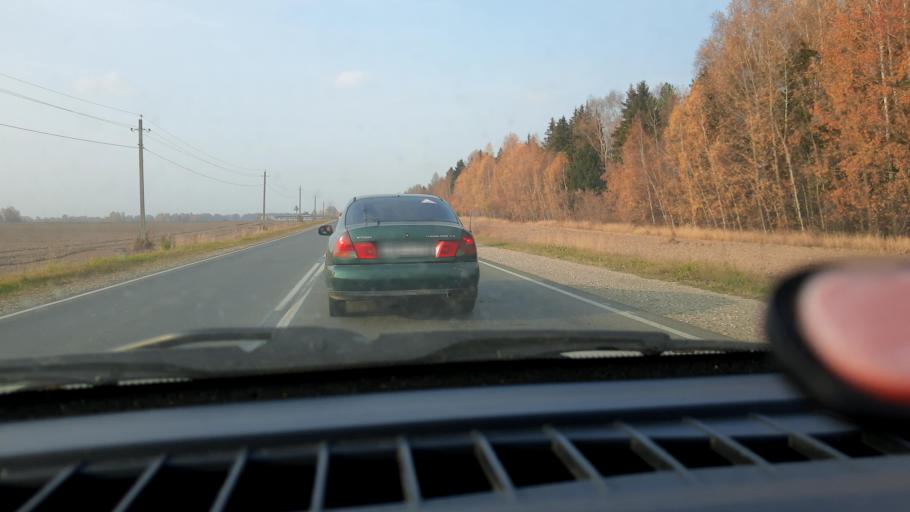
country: RU
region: Nizjnij Novgorod
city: Gorodets
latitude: 56.6181
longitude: 43.5579
